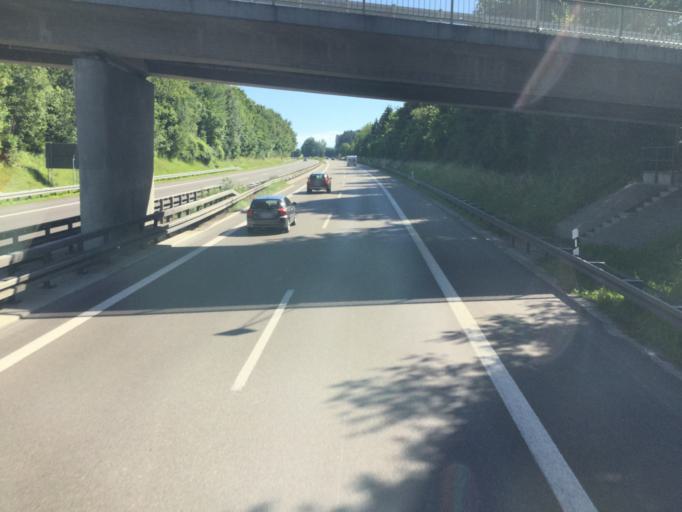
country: DE
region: Baden-Wuerttemberg
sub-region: Tuebingen Region
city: Neukirch
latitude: 47.6403
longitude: 9.7443
